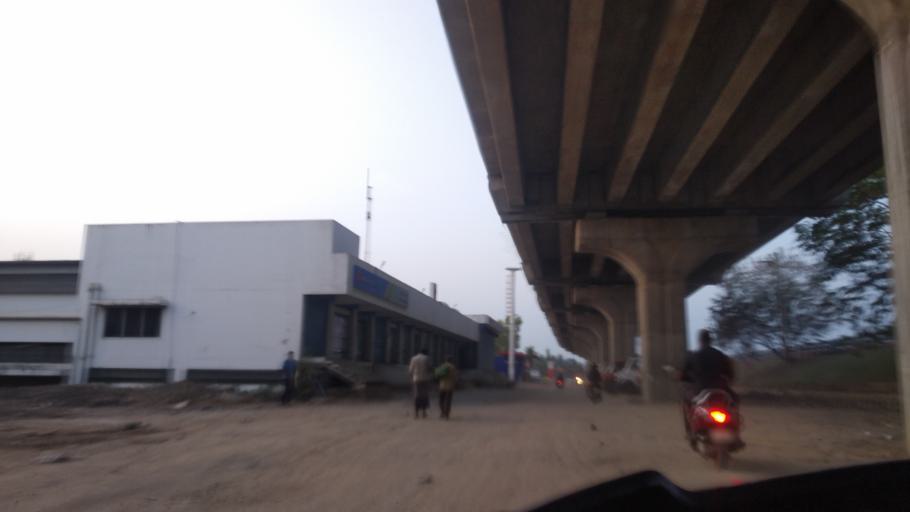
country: IN
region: Tamil Nadu
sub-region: Coimbatore
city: Coimbatore
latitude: 10.9848
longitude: 76.9617
